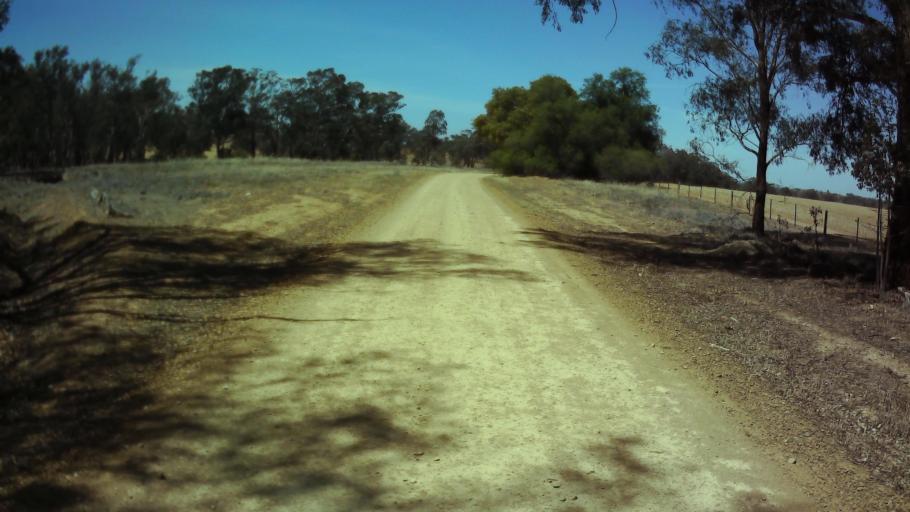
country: AU
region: New South Wales
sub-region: Weddin
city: Grenfell
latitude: -33.9214
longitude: 148.1953
